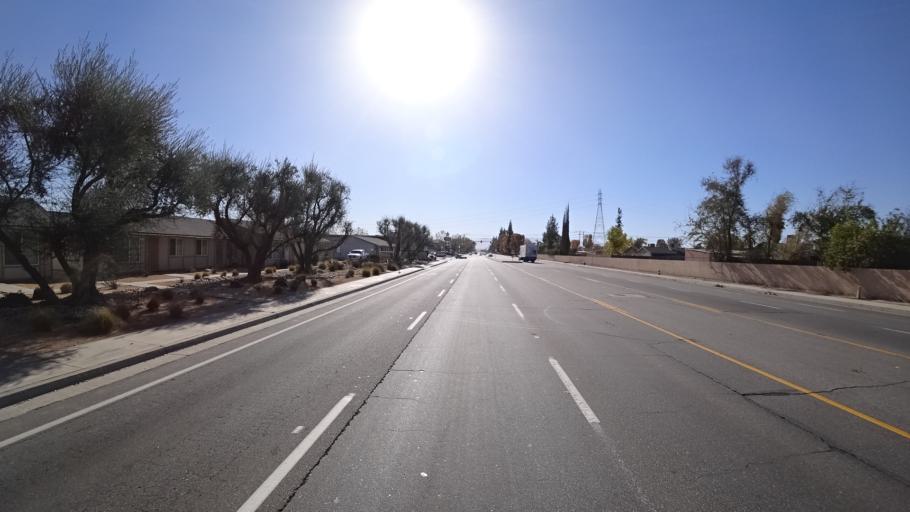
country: US
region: California
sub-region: Kern County
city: Bakersfield
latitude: 35.3198
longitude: -119.0566
